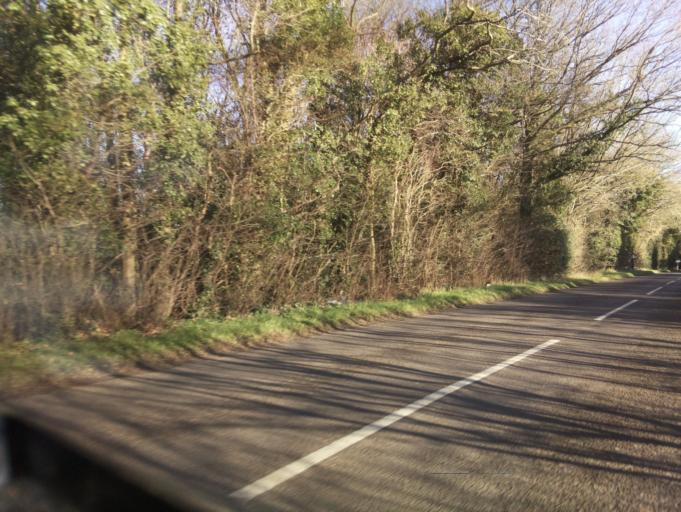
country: GB
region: England
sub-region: Staffordshire
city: Barton under Needwood
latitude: 52.8175
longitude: -1.7584
